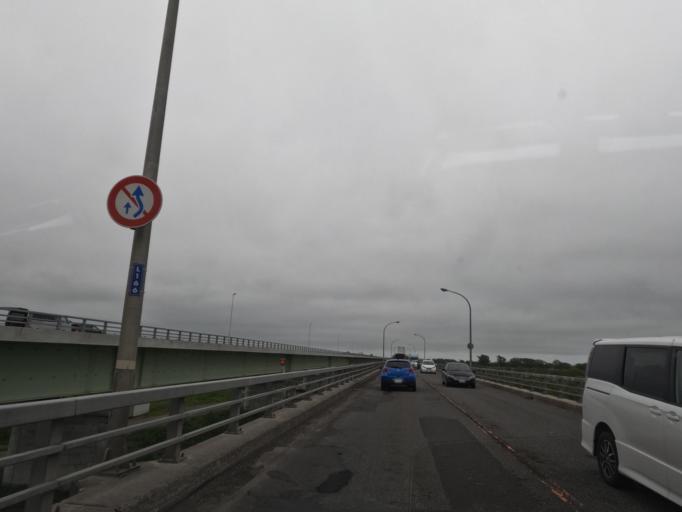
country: JP
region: Hokkaido
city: Ebetsu
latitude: 43.1321
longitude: 141.5082
